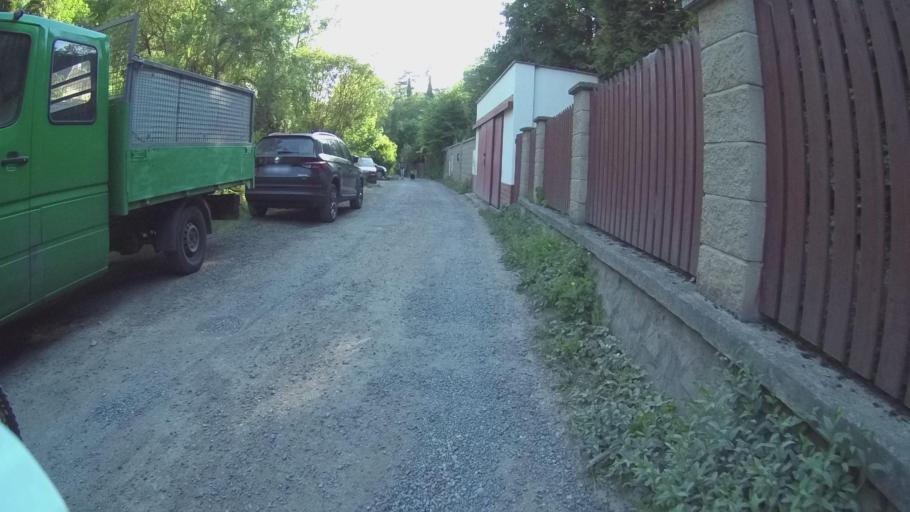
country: CZ
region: Central Bohemia
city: Roztoky
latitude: 50.1494
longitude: 14.4189
